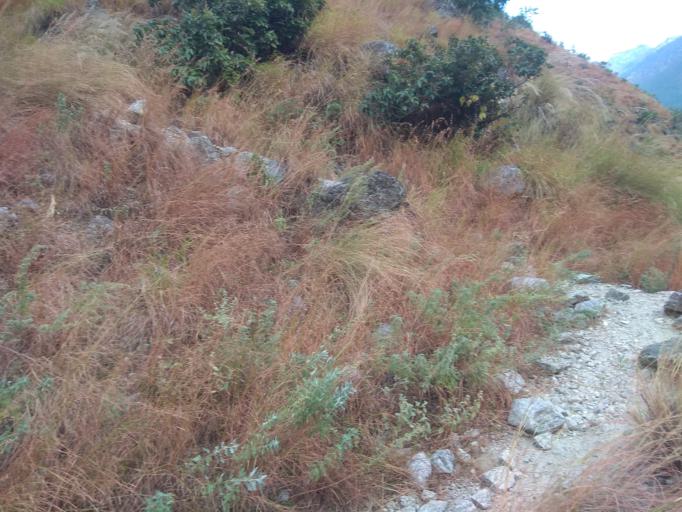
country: NP
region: Far Western
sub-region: Seti Zone
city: Achham
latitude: 29.2208
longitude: 81.6320
